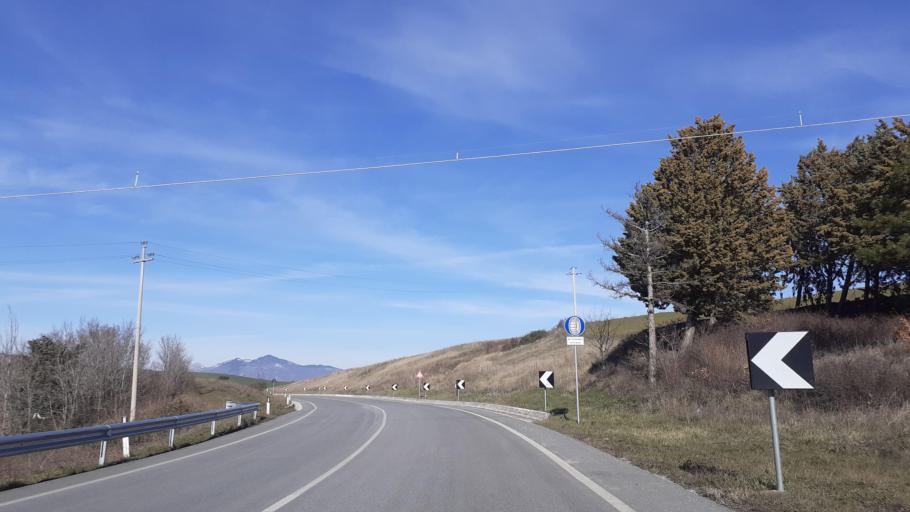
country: IT
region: Molise
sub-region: Provincia di Campobasso
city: Pietracupa
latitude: 41.6827
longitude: 14.5140
